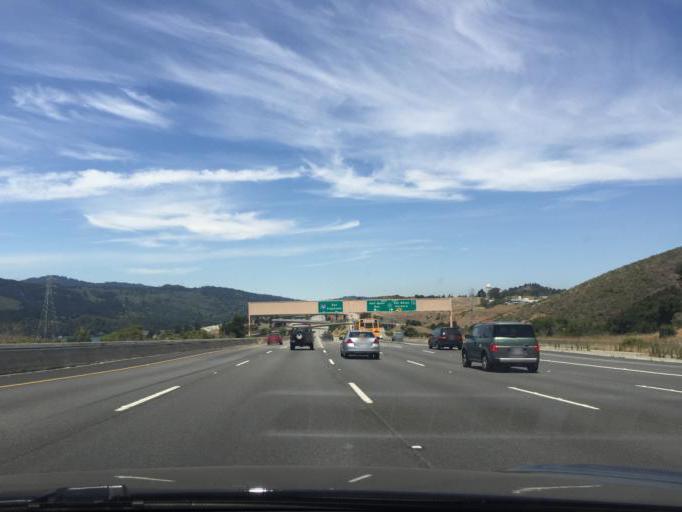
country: US
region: California
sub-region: San Mateo County
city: Highlands-Baywood Park
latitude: 37.5024
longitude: -122.3307
